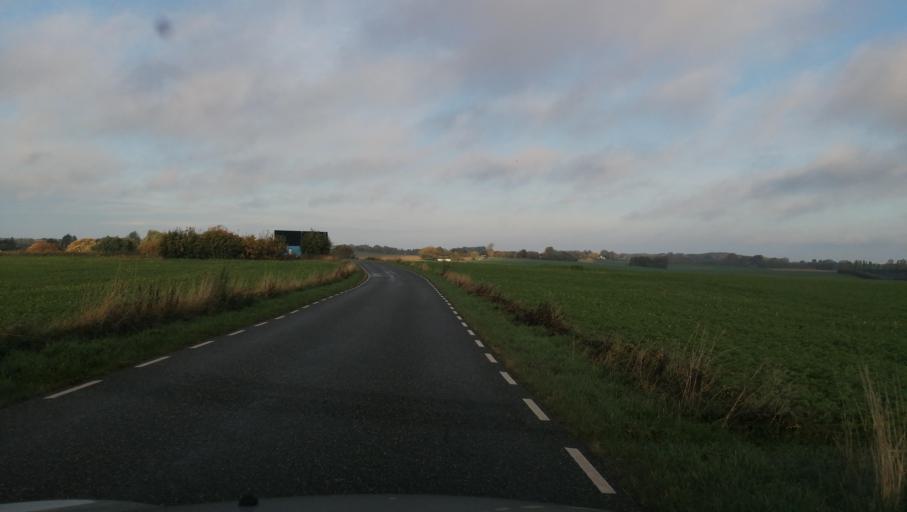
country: DK
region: Zealand
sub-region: Odsherred Kommune
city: Horve
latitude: 55.7446
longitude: 11.3898
